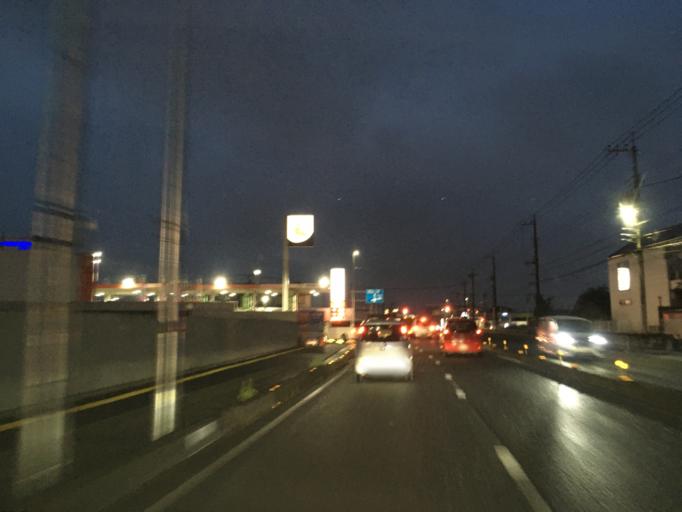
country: JP
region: Saitama
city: Shiki
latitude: 35.8080
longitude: 139.5503
